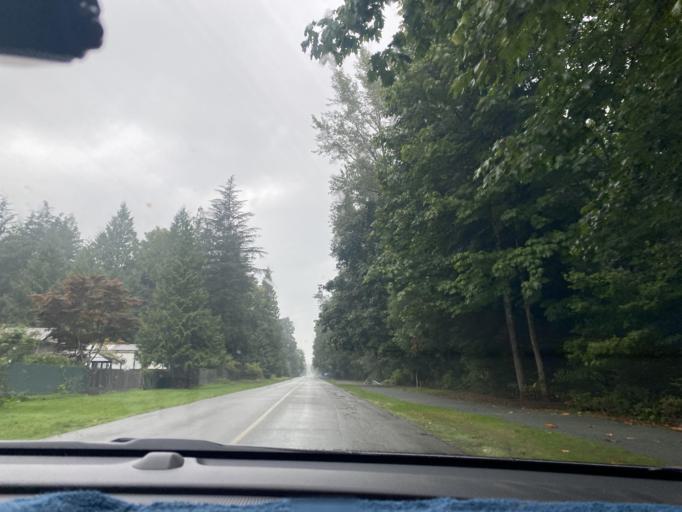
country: CA
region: British Columbia
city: Agassiz
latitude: 49.2823
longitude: -121.7775
